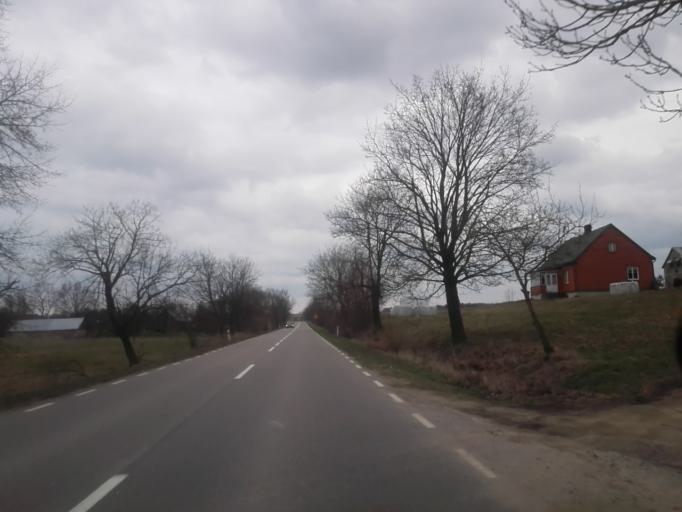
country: PL
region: Podlasie
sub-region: Powiat sejnenski
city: Sejny
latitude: 54.0899
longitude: 23.3459
